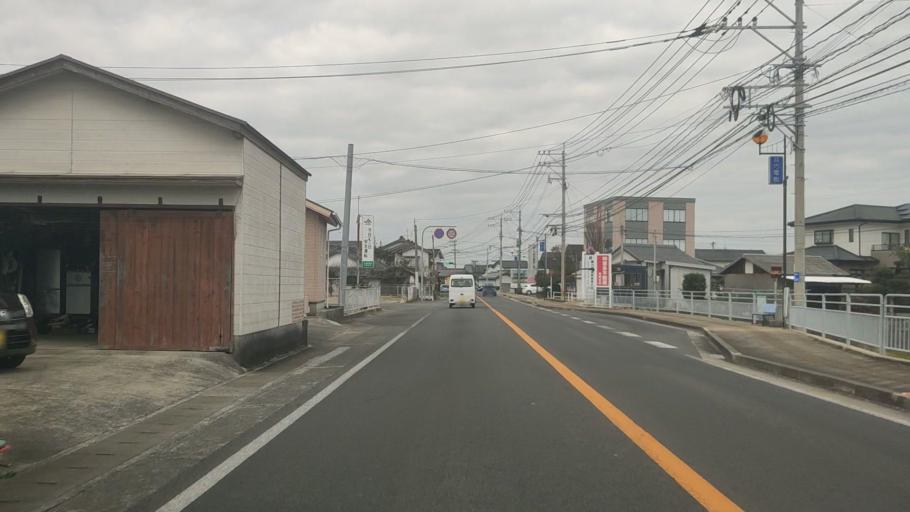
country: JP
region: Nagasaki
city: Shimabara
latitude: 32.8579
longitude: 130.3353
